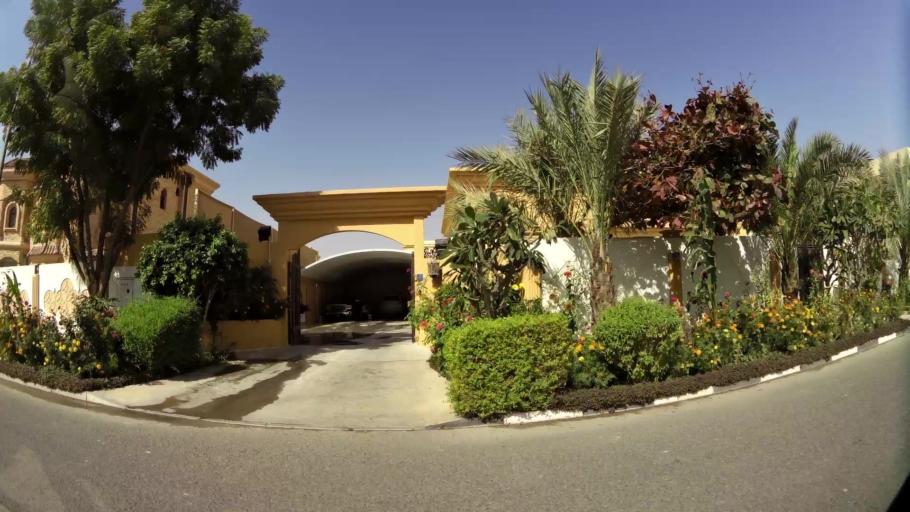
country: QA
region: Baladiyat ad Dawhah
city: Doha
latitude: 25.3598
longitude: 51.5149
